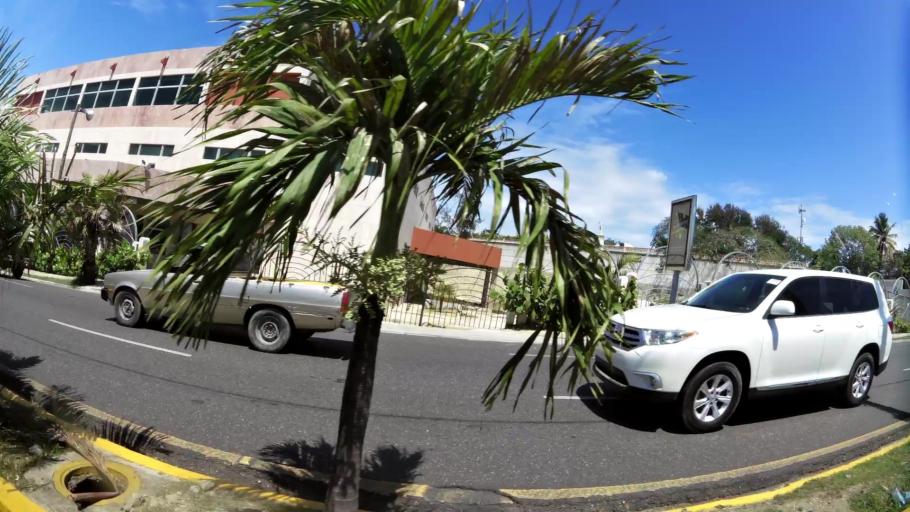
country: DO
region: Santiago
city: Santiago de los Caballeros
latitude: 19.4527
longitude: -70.6942
